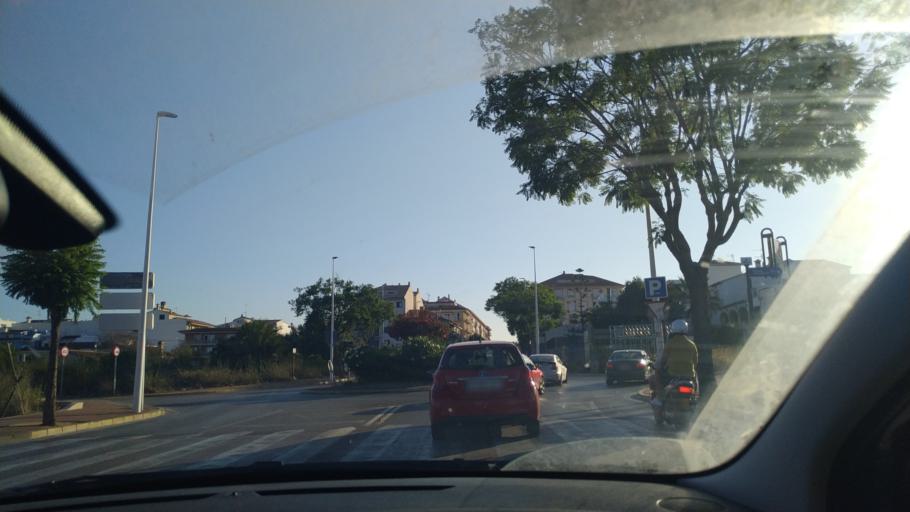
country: ES
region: Valencia
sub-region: Provincia de Alicante
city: Javea
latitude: 38.7867
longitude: 0.1658
